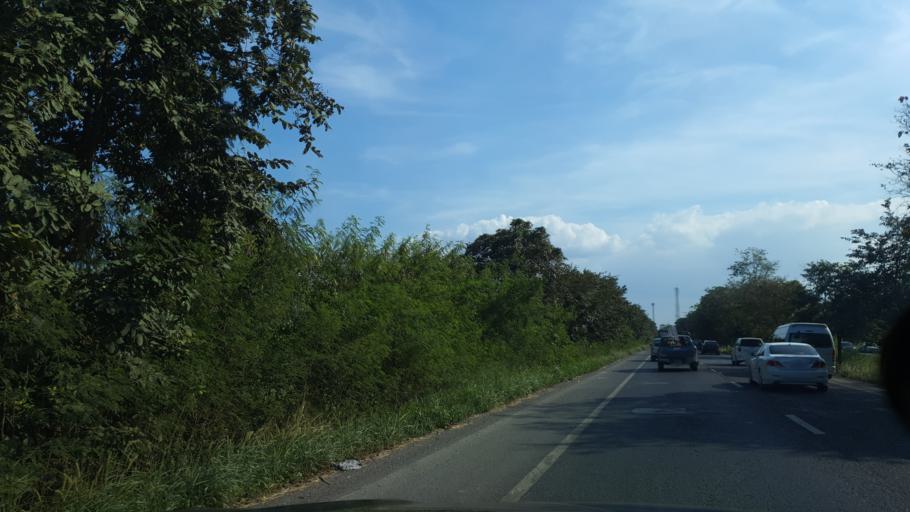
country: TH
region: Surat Thani
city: Ban Na Doem
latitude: 8.9775
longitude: 99.2246
